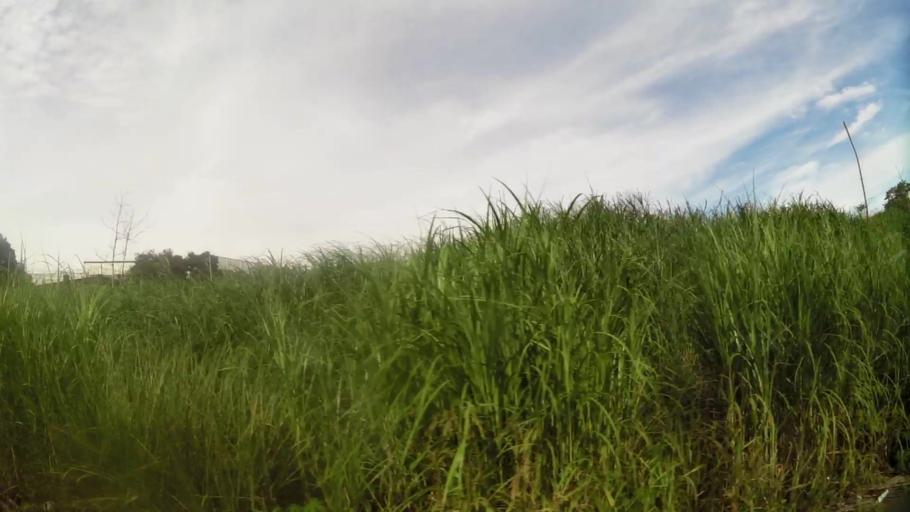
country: PA
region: Panama
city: La Chorrera
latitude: 8.8868
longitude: -79.7702
